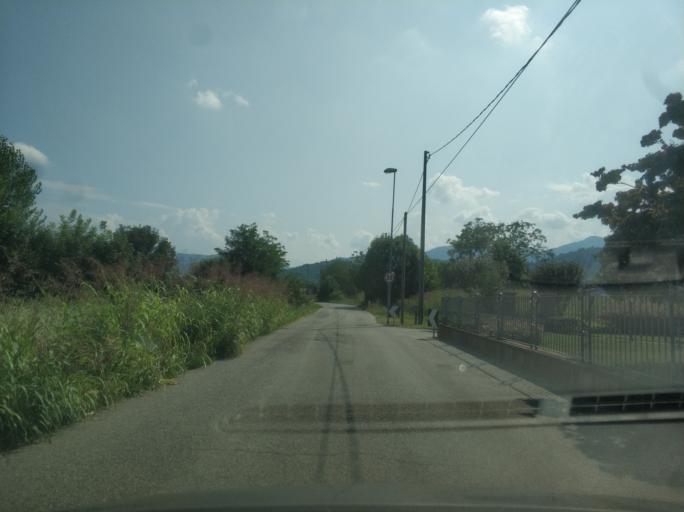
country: IT
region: Piedmont
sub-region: Provincia di Cuneo
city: Caraglio
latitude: 44.4365
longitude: 7.4313
